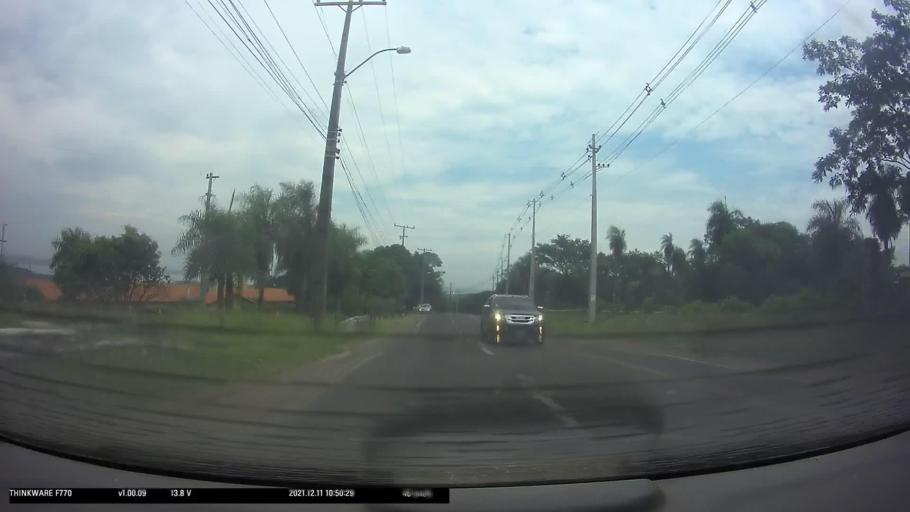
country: PY
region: Cordillera
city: San Bernardino
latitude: -25.2986
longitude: -57.2758
